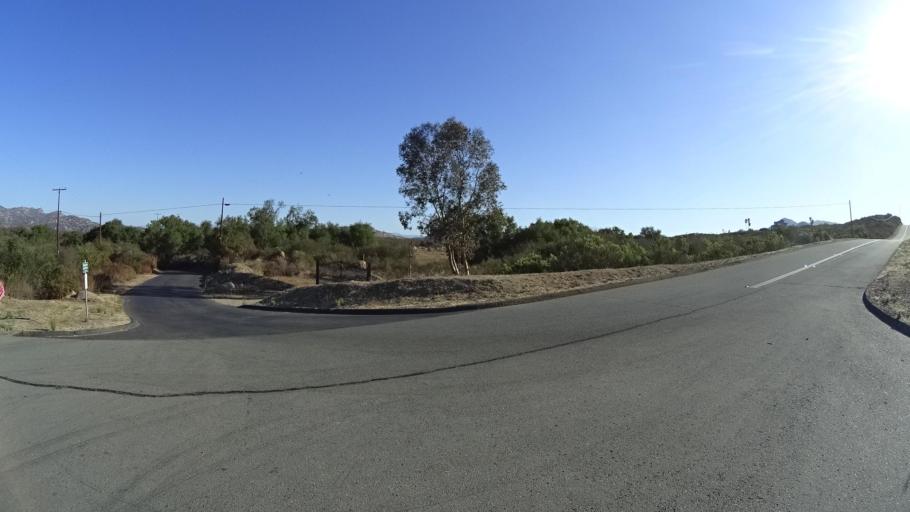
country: US
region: California
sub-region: San Diego County
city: Eucalyptus Hills
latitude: 32.9062
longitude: -116.9118
